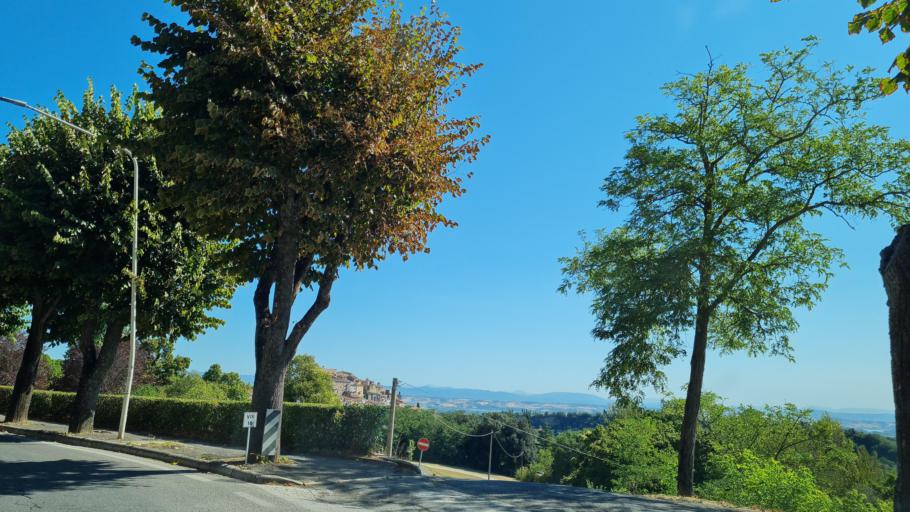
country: IT
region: Tuscany
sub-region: Provincia di Siena
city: Chianciano Terme
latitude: 43.0534
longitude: 11.8230
